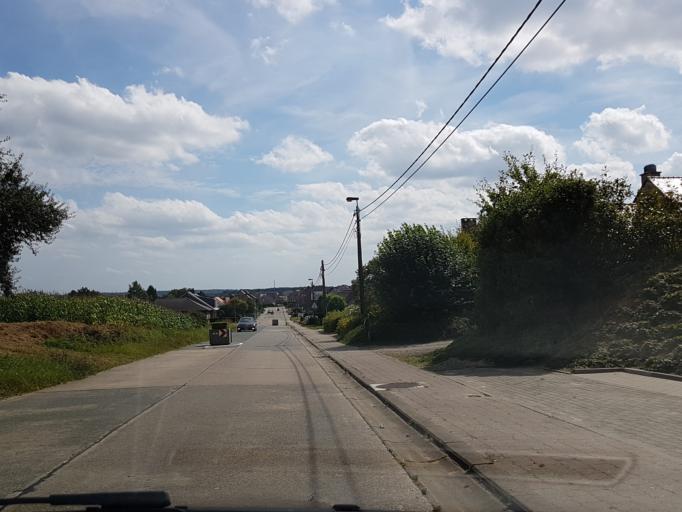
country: BE
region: Flanders
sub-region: Provincie Vlaams-Brabant
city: Bertem
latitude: 50.8753
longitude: 4.6283
